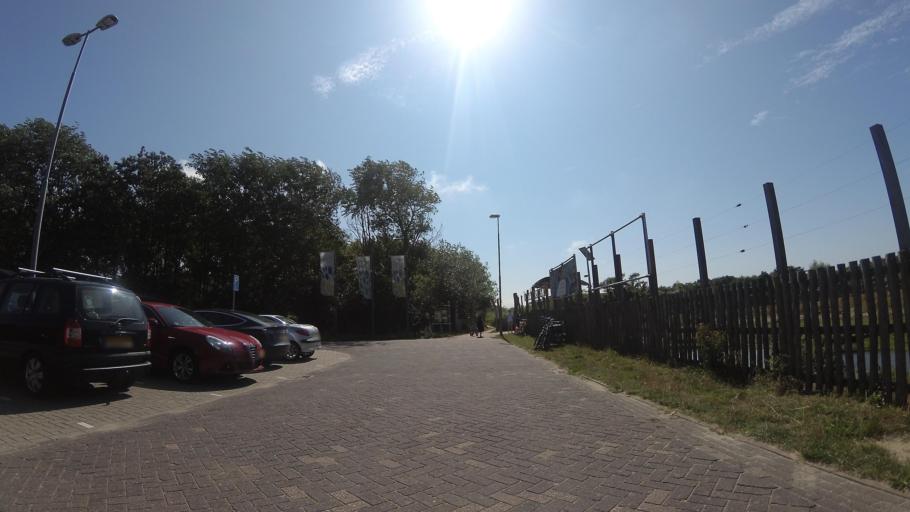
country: NL
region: North Holland
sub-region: Gemeente Den Helder
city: Den Helder
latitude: 52.9347
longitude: 4.7330
